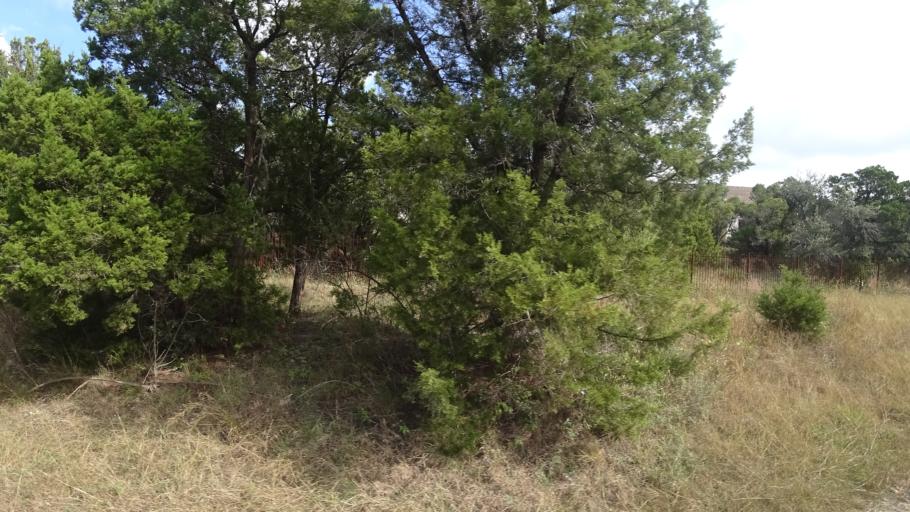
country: US
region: Texas
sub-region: Travis County
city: Barton Creek
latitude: 30.3105
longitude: -97.8806
